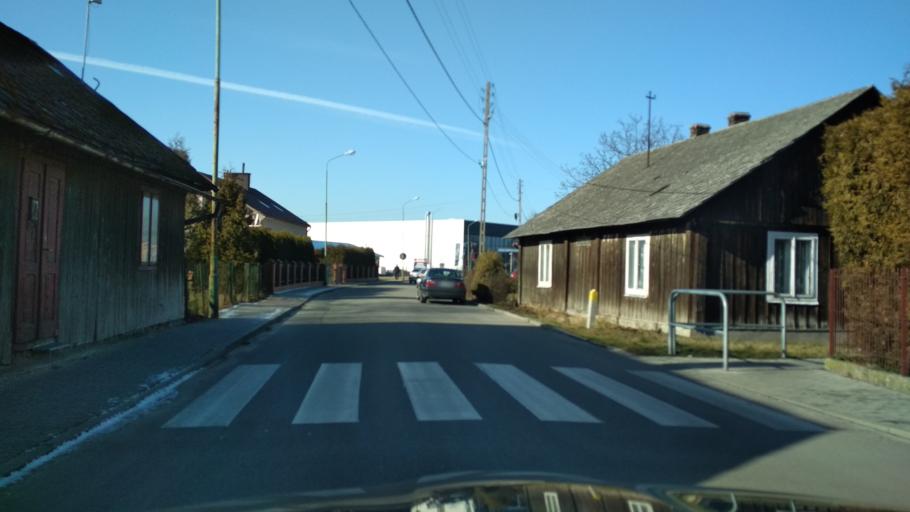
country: PL
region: Subcarpathian Voivodeship
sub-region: Powiat ropczycko-sedziszowski
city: Sedziszow Malopolski
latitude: 50.0718
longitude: 21.6963
